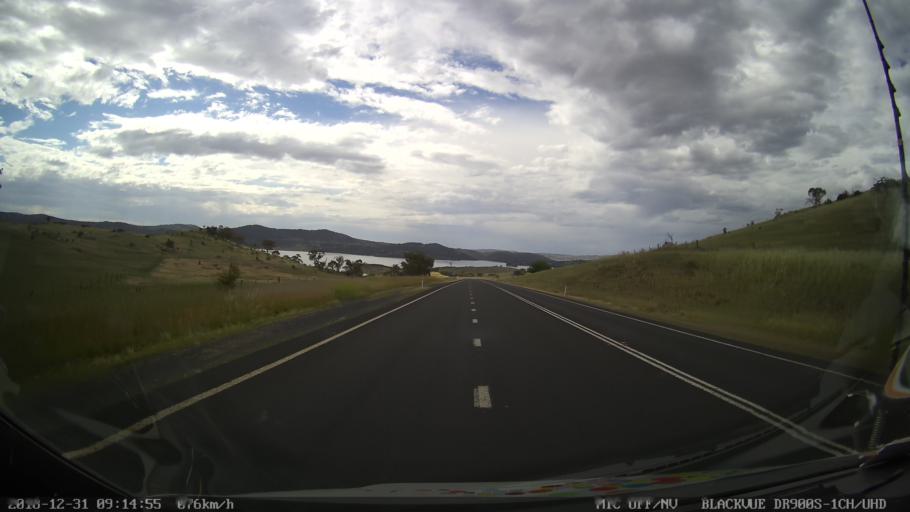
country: AU
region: New South Wales
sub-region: Snowy River
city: Jindabyne
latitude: -36.3797
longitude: 148.5956
